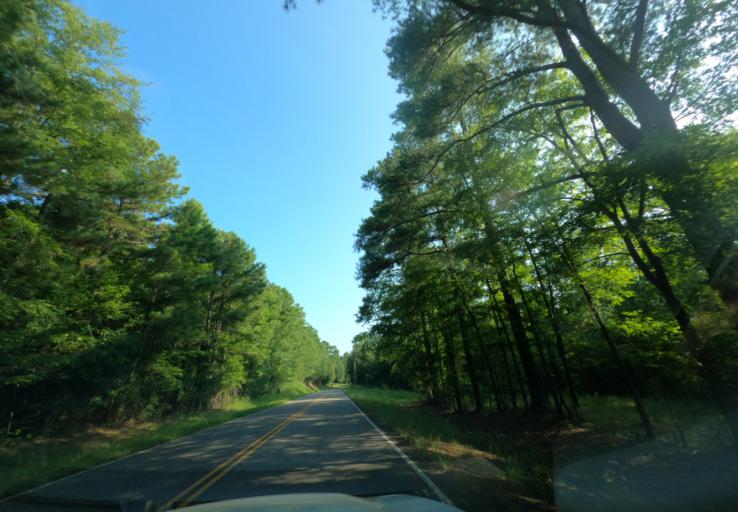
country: US
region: South Carolina
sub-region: Edgefield County
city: Murphys Estates
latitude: 33.6404
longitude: -81.9779
